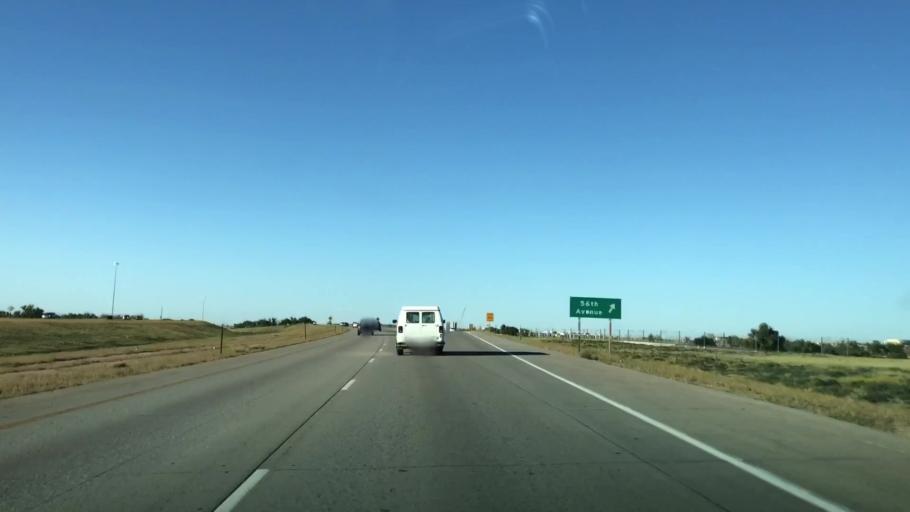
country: US
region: Colorado
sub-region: Adams County
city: Aurora
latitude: 39.7935
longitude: -104.7875
